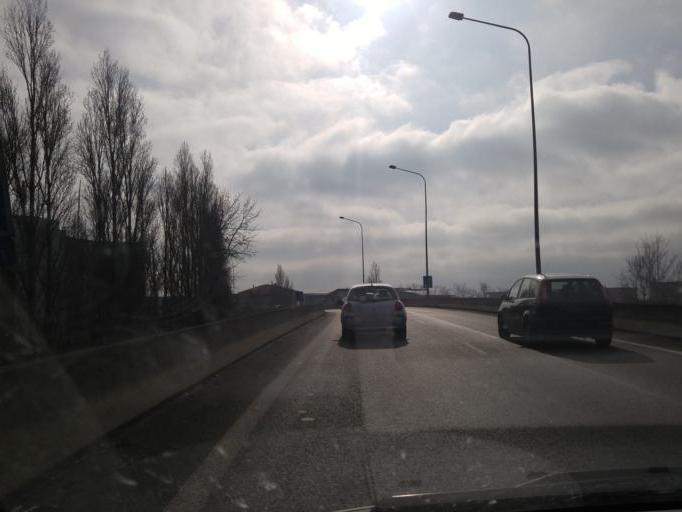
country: FR
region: Midi-Pyrenees
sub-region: Departement de la Haute-Garonne
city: Blagnac
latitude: 43.6340
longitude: 1.3794
